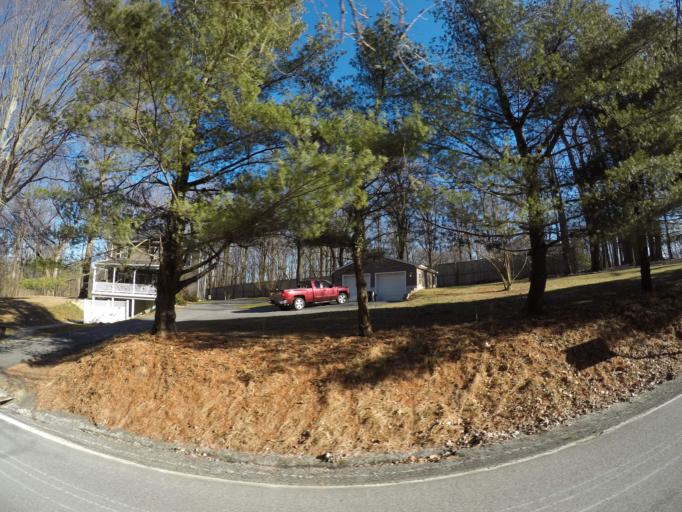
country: US
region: Maryland
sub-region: Howard County
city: Ilchester
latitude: 39.2318
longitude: -76.7852
